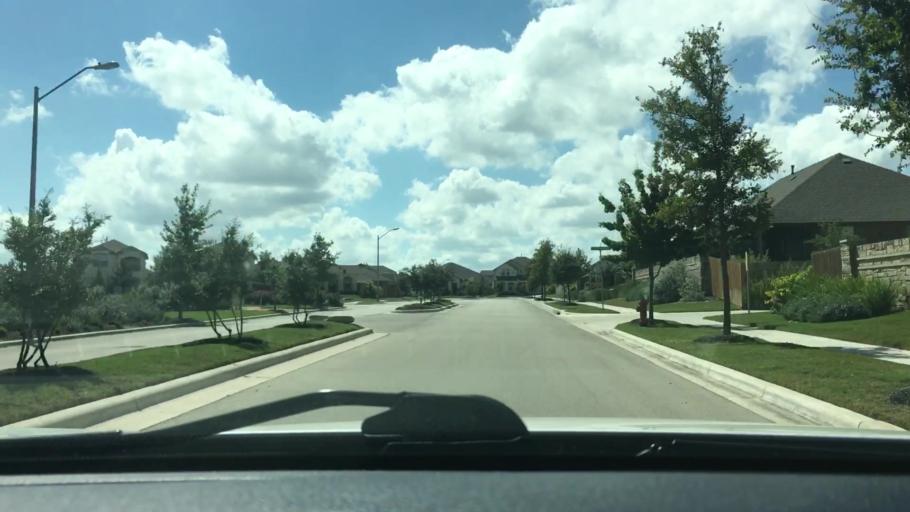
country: US
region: Texas
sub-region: Travis County
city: Windemere
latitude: 30.4804
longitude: -97.6530
